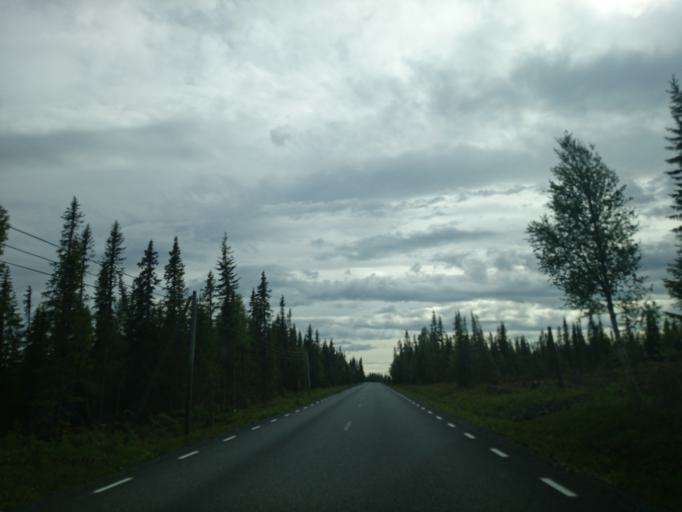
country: SE
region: Jaemtland
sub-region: Are Kommun
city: Are
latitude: 63.2524
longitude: 13.2039
